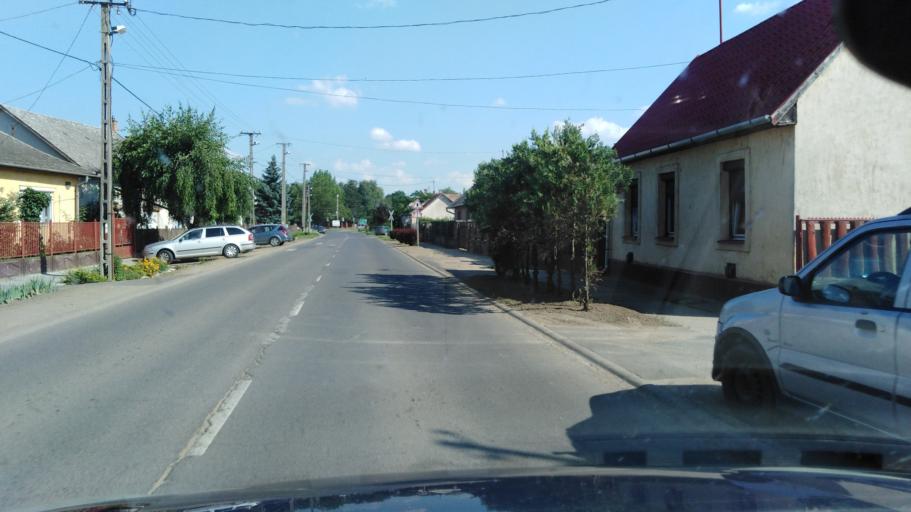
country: HU
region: Szabolcs-Szatmar-Bereg
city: Nyirbator
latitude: 47.8279
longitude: 22.1420
